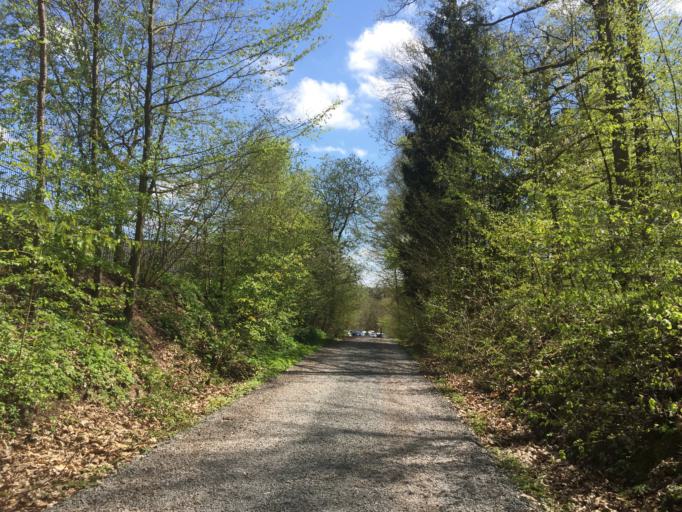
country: DE
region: Bavaria
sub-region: Regierungsbezirk Unterfranken
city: Sulzfeld
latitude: 50.2450
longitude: 10.4589
